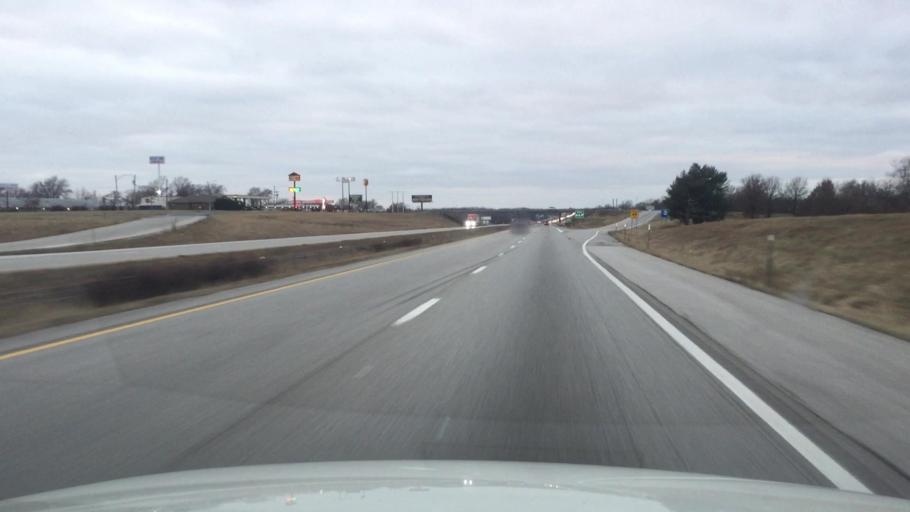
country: US
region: Missouri
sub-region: Saline County
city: Sweet Springs
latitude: 38.9772
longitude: -93.4114
